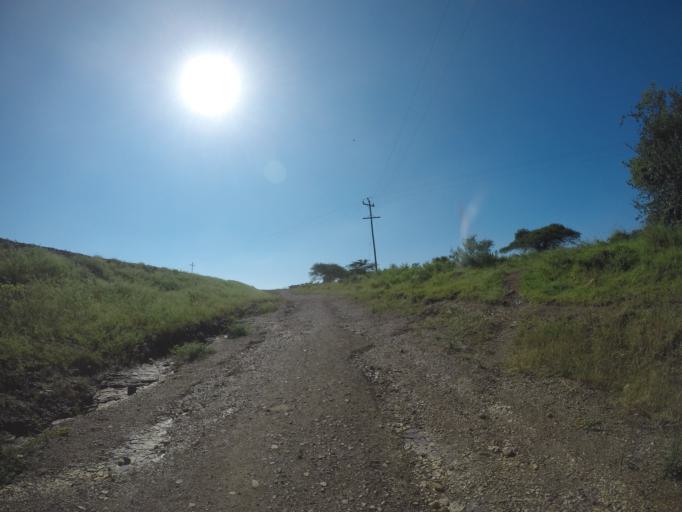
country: ZA
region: KwaZulu-Natal
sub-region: uThungulu District Municipality
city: Empangeni
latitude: -28.5716
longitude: 31.7172
